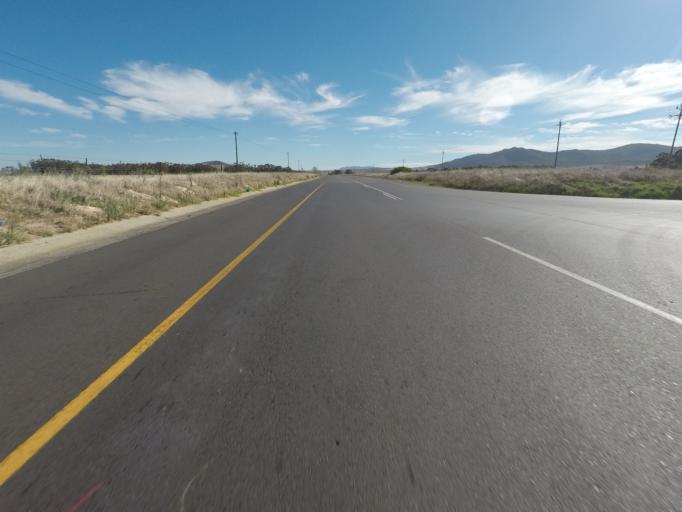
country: ZA
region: Western Cape
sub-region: West Coast District Municipality
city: Malmesbury
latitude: -33.6219
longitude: 18.7255
